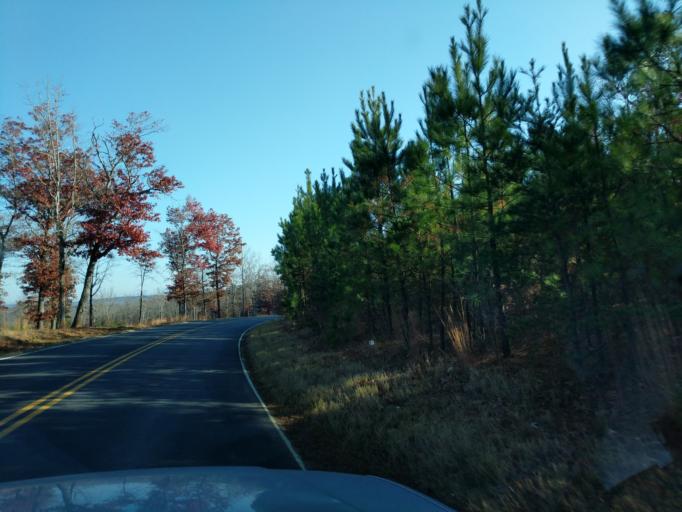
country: US
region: North Carolina
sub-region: Polk County
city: Columbus
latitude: 35.2615
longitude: -82.0633
